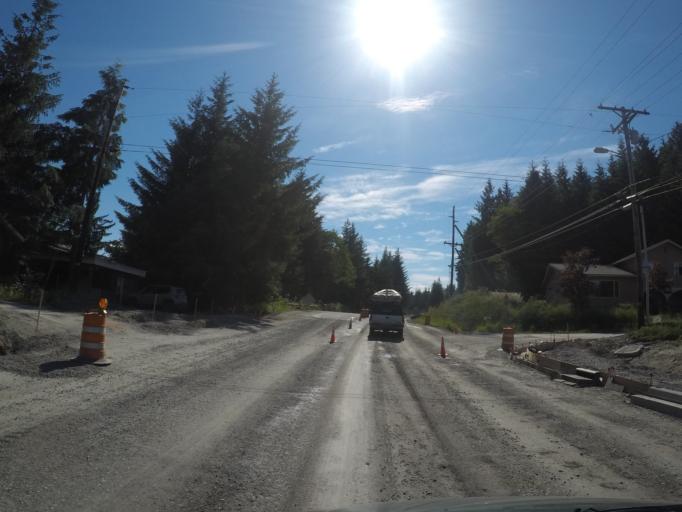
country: US
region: Alaska
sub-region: Juneau City and Borough
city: Juneau
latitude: 58.3865
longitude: -134.6543
